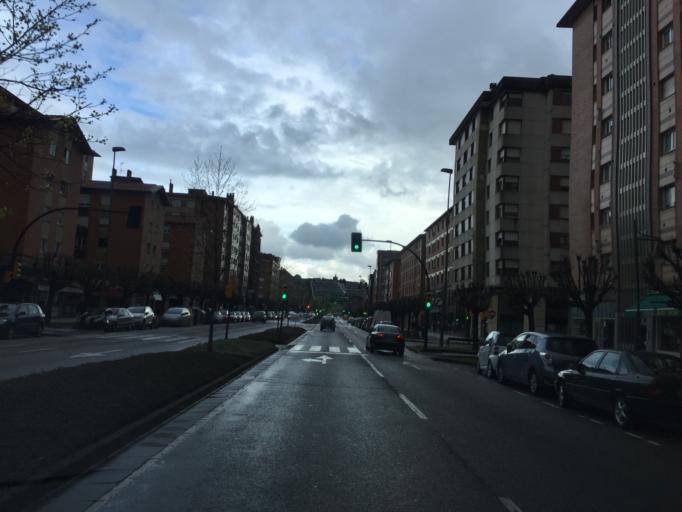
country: ES
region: Asturias
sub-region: Province of Asturias
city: Gijon
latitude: 43.5262
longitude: -5.6706
